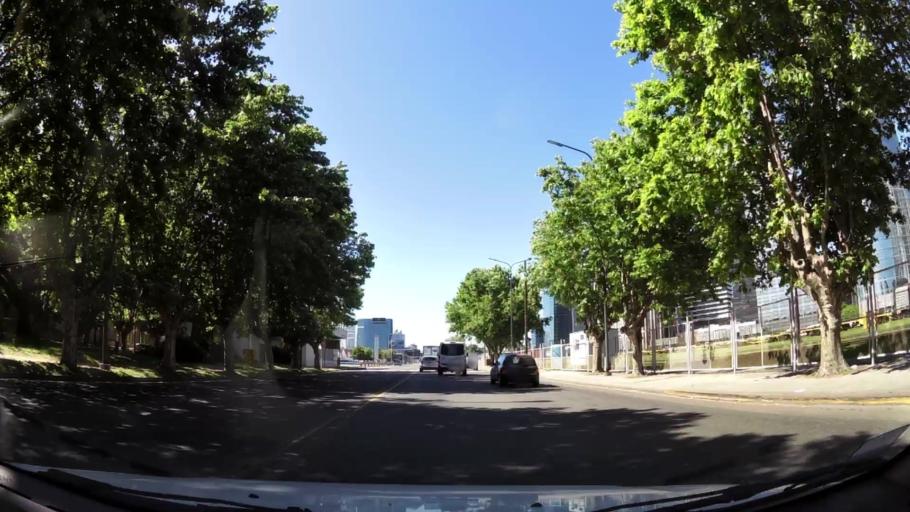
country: AR
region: Buenos Aires F.D.
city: Retiro
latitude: -34.5928
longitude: -58.3701
